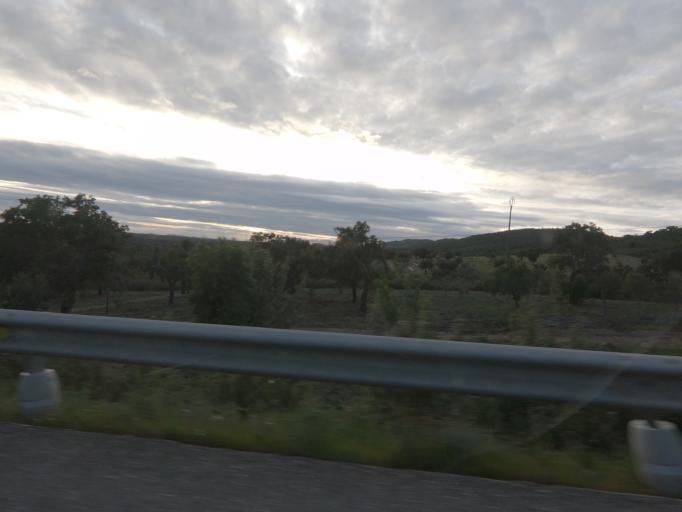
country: ES
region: Extremadura
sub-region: Provincia de Badajoz
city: Puebla de Obando
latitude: 39.1608
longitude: -6.6417
